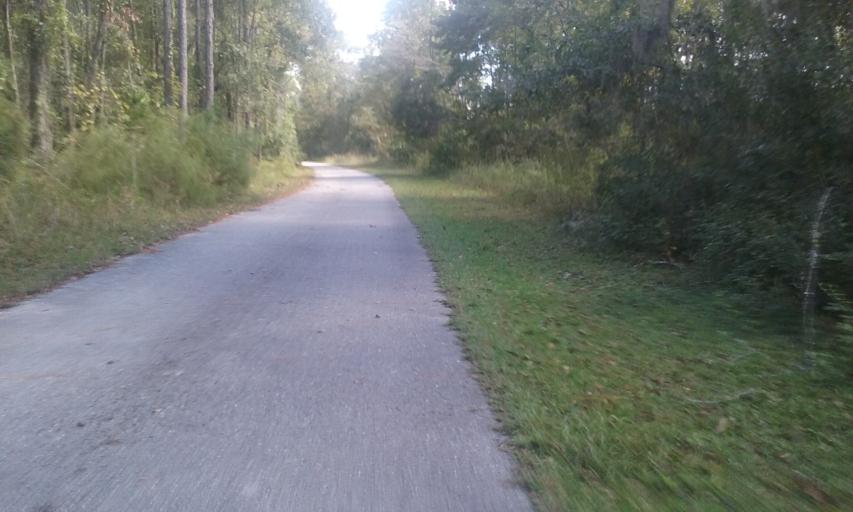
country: US
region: Florida
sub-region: Alachua County
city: Hawthorne
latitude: 29.5902
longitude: -82.1819
